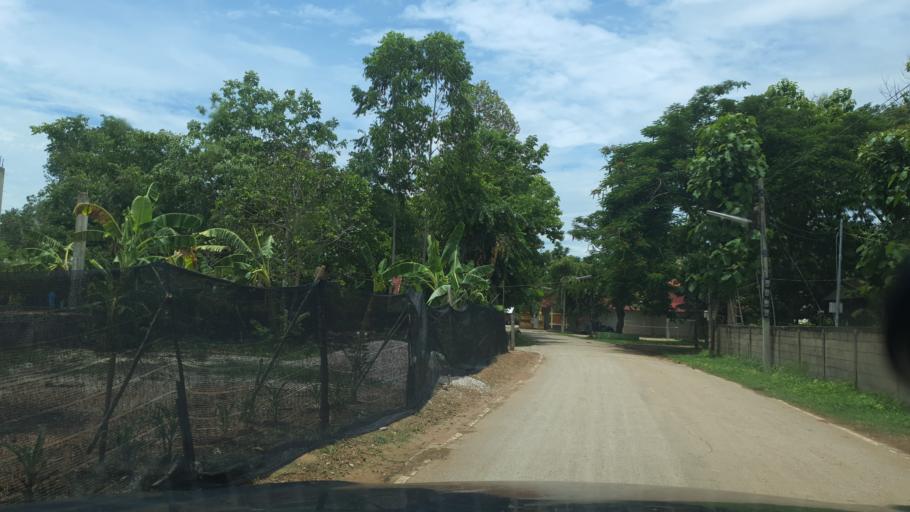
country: TH
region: Lampang
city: Ko Kha
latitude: 18.1986
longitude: 99.3293
